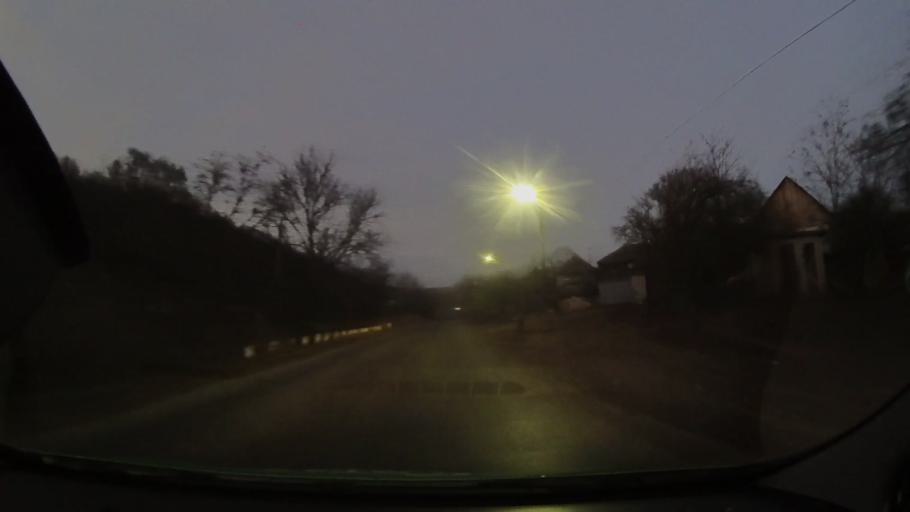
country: RO
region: Constanta
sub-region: Comuna Ion Corvin
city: Ion Corvin
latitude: 44.1160
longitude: 27.8108
